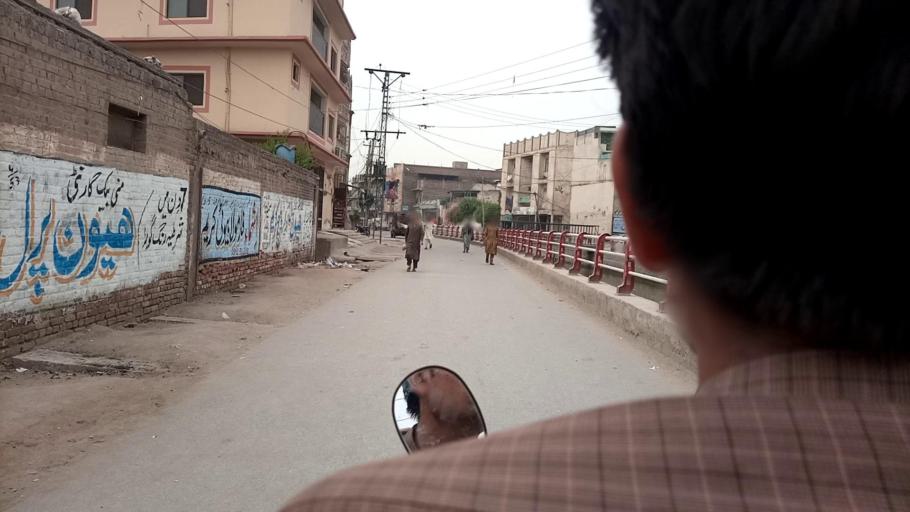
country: PK
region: Khyber Pakhtunkhwa
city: Peshawar
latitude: 34.0209
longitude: 71.5925
